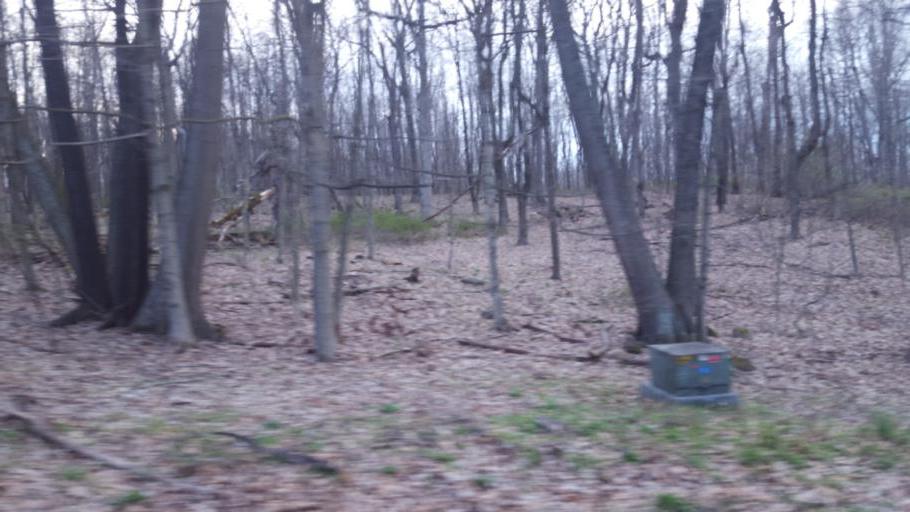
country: US
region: Ohio
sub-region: Knox County
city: Danville
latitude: 40.4654
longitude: -82.3450
